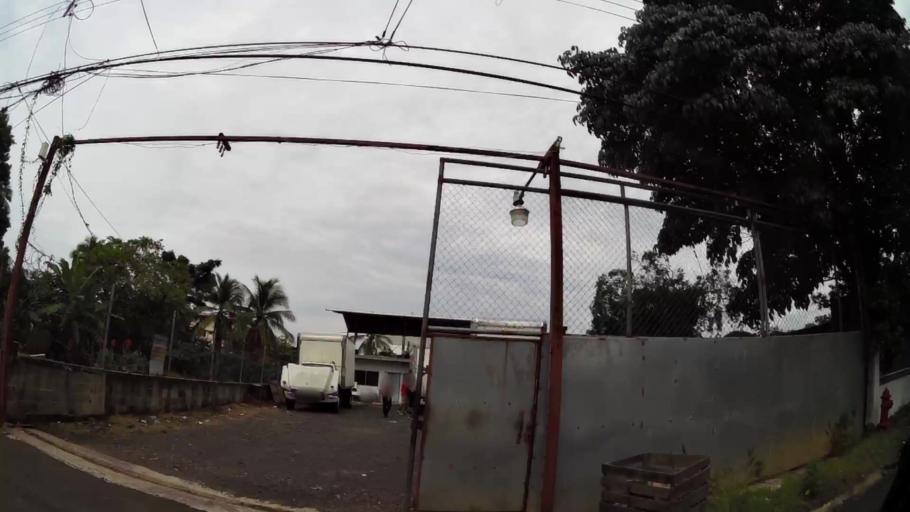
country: PA
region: Panama
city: San Miguelito
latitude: 9.0492
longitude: -79.4358
